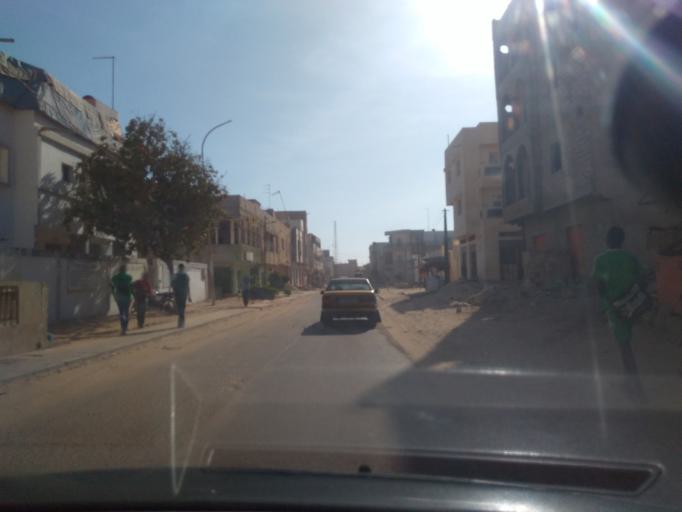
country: SN
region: Dakar
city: Grand Dakar
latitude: 14.7630
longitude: -17.4459
